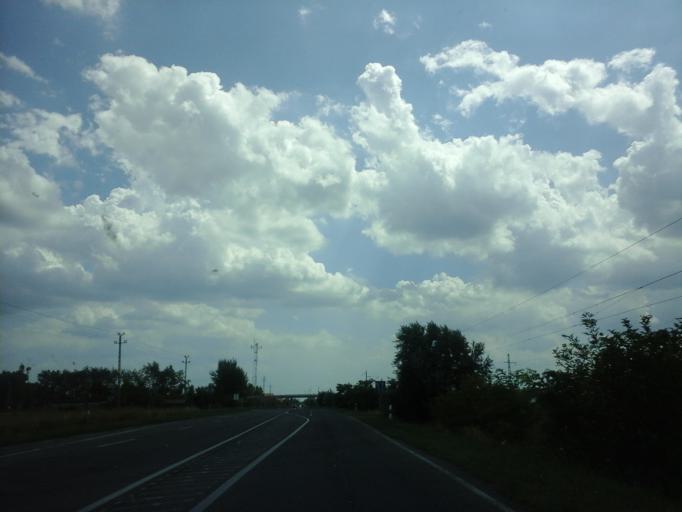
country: HU
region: Gyor-Moson-Sopron
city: Rajka
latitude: 48.0078
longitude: 17.1838
